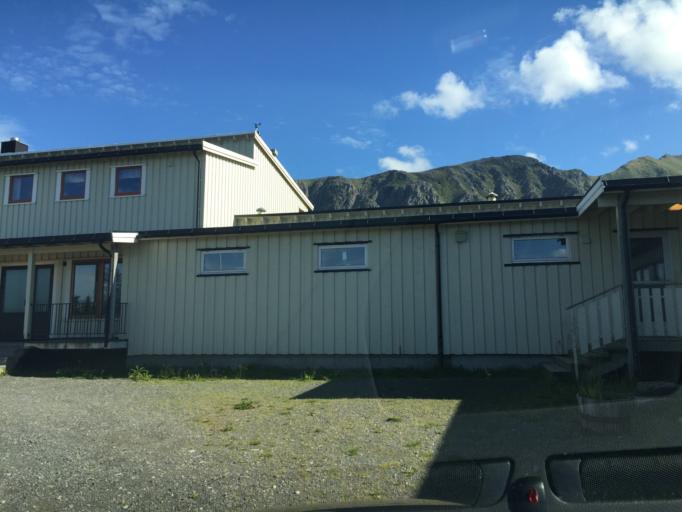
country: NO
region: Nordland
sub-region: Vagan
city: Kabelvag
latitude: 68.3905
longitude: 14.4713
